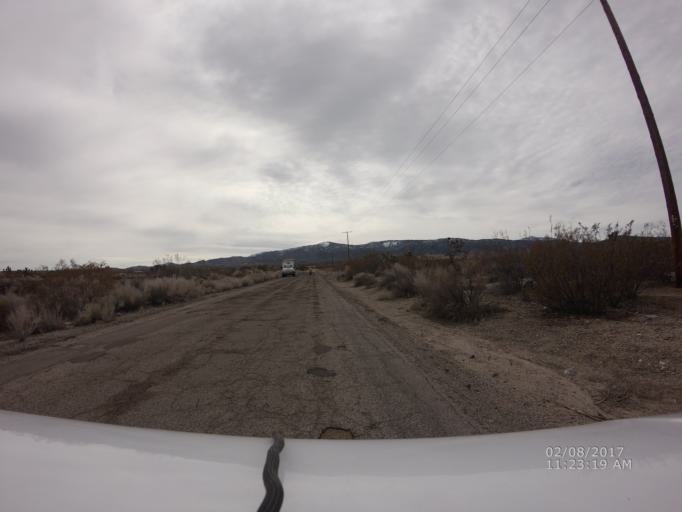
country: US
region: California
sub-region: San Bernardino County
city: Pinon Hills
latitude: 34.4577
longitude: -117.6598
